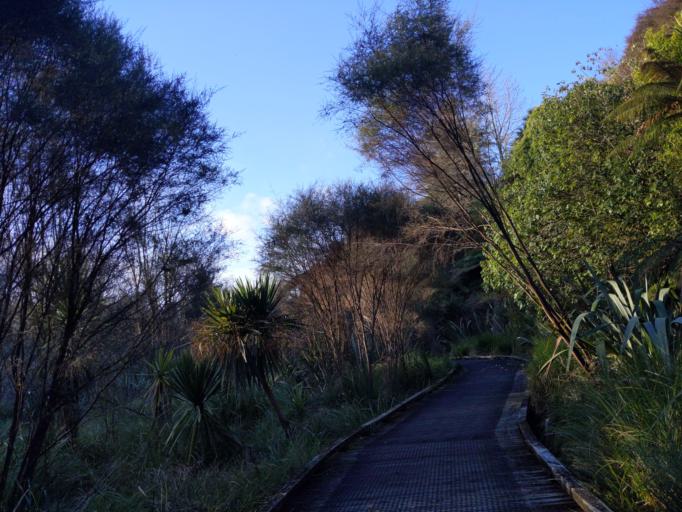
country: NZ
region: Waikato
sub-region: Hamilton City
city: Hamilton
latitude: -37.7401
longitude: 175.2755
